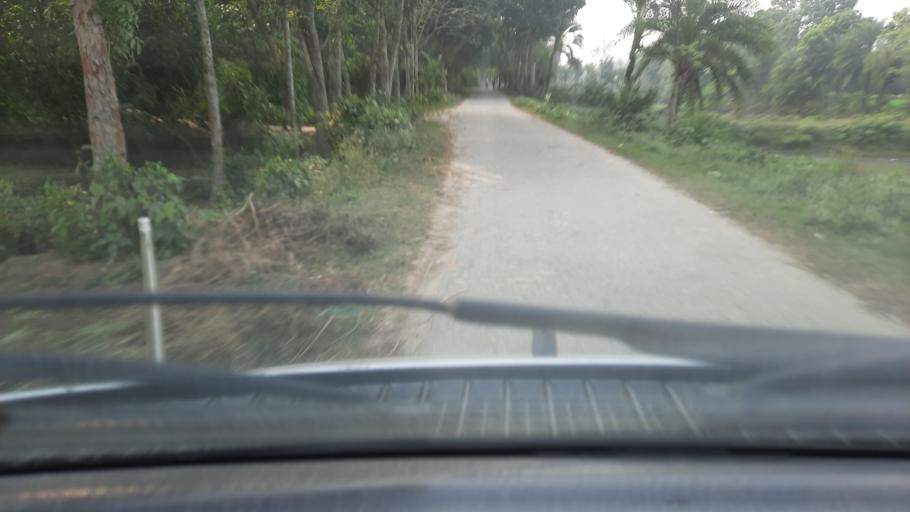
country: BD
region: Khulna
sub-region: Chuadanga
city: Nowlamary
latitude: 23.5998
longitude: 88.8462
